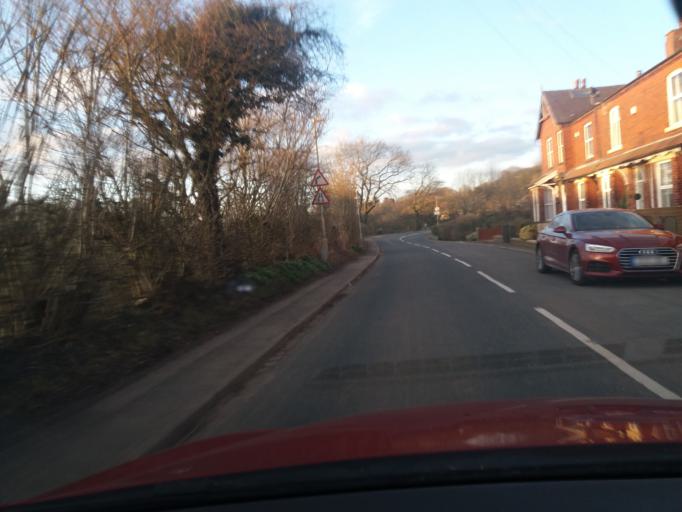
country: GB
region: England
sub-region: Lancashire
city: Chorley
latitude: 53.6779
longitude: -2.6212
